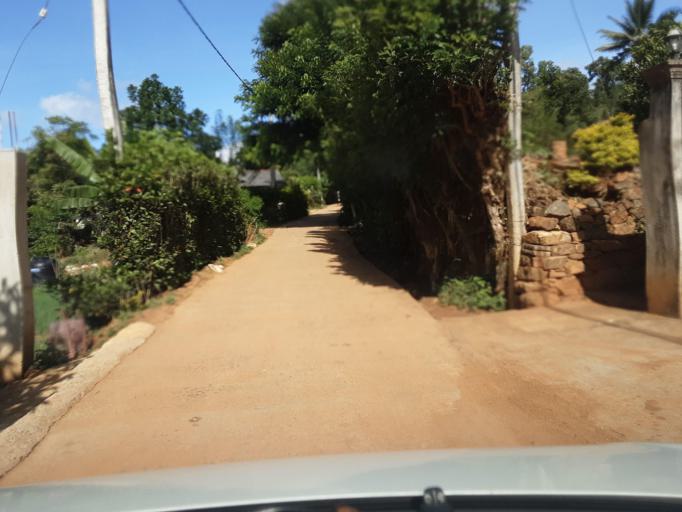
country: LK
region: Uva
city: Haputale
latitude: 6.8946
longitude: 80.9195
